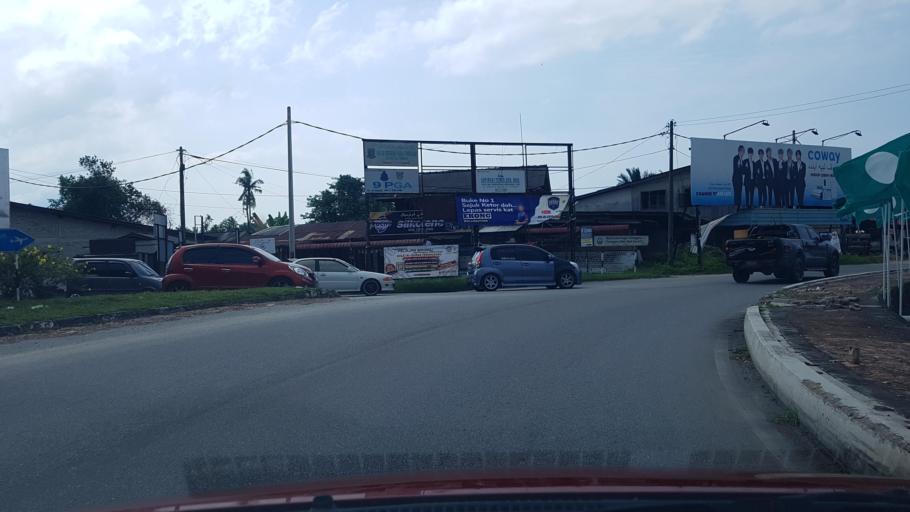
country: MY
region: Terengganu
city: Kuala Terengganu
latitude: 5.3474
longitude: 103.0922
